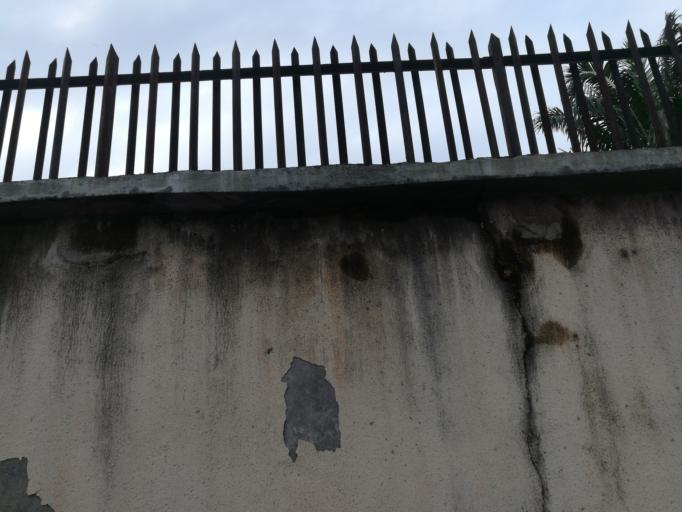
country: NG
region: Rivers
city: Port Harcourt
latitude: 4.8423
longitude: 7.0486
